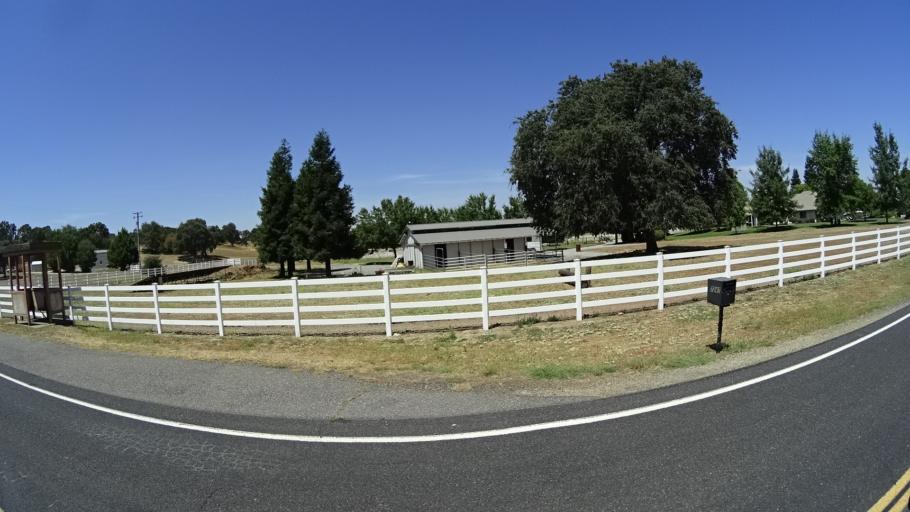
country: US
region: California
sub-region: Calaveras County
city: Rancho Calaveras
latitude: 38.1597
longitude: -120.9434
